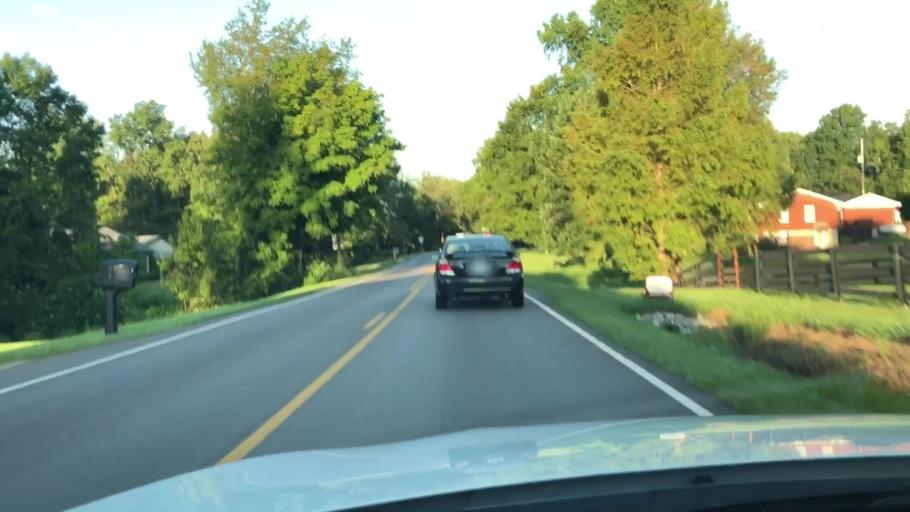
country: US
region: Kentucky
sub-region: Jefferson County
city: Middletown
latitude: 38.2182
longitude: -85.5236
